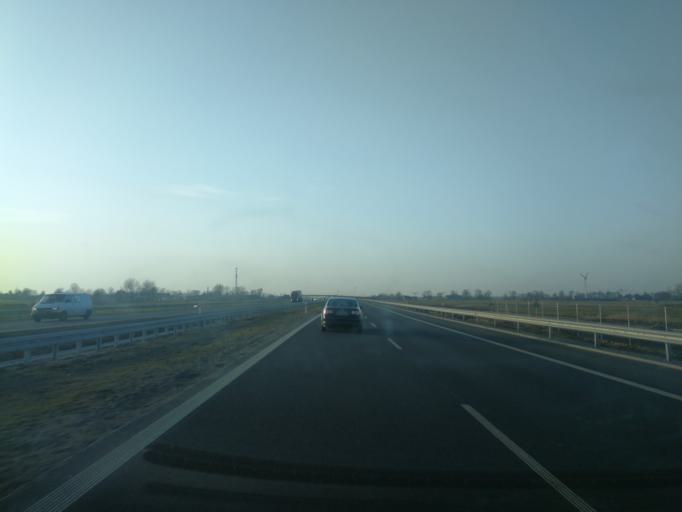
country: PL
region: Pomeranian Voivodeship
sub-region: Powiat nowodworski
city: Ostaszewo
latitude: 54.2461
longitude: 18.9951
